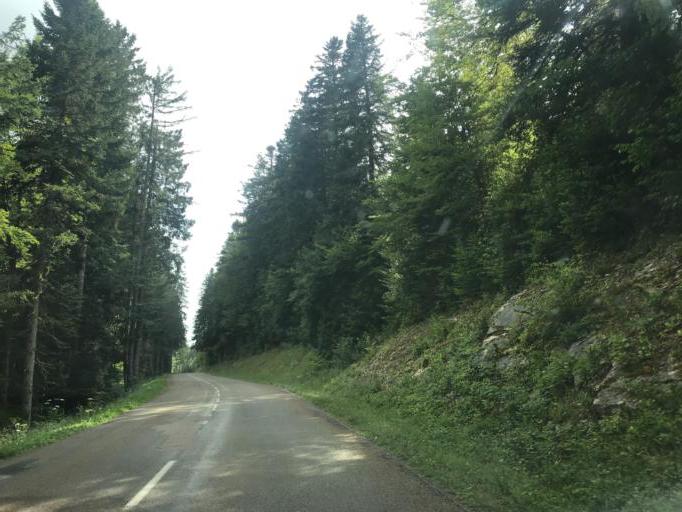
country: FR
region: Franche-Comte
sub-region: Departement du Jura
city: Valfin-les-Saint-Claude
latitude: 46.4892
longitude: 5.8449
